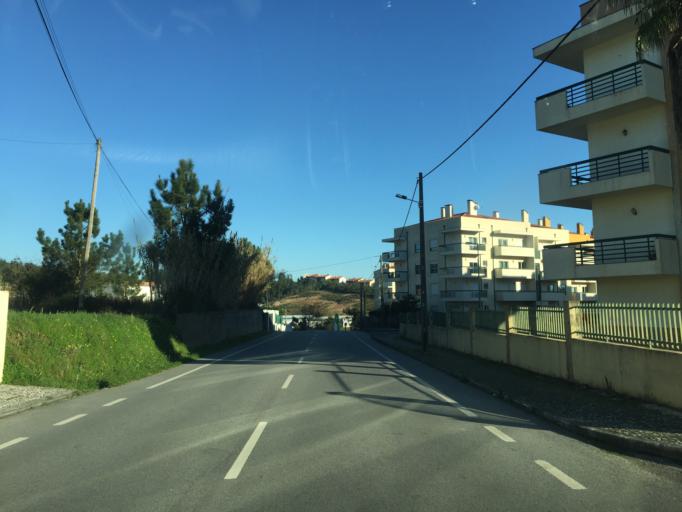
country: PT
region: Coimbra
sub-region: Figueira da Foz
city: Tavarede
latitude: 40.1652
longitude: -8.8315
